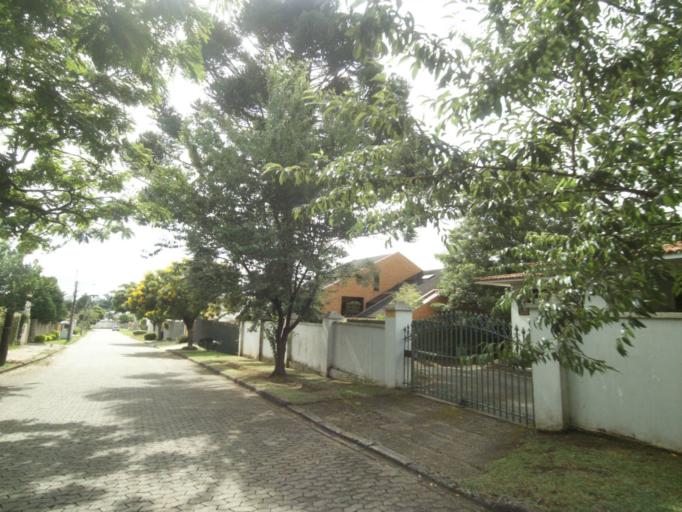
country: BR
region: Parana
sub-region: Curitiba
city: Curitiba
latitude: -25.4410
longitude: -49.3020
